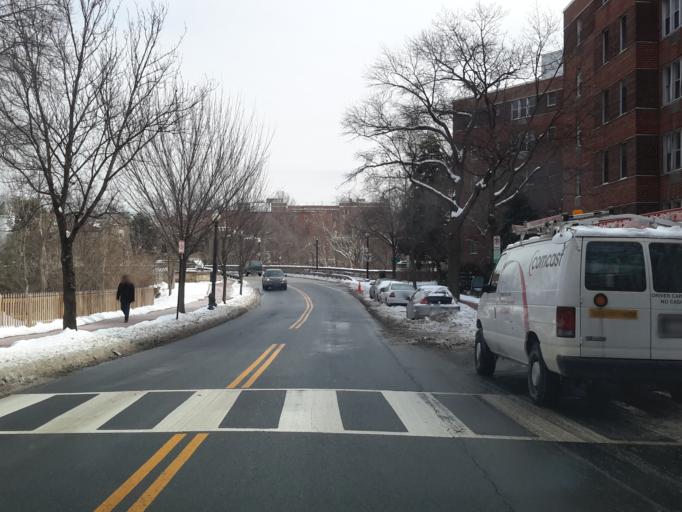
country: US
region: Washington, D.C.
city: Washington, D.C.
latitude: 38.9106
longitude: -77.0526
